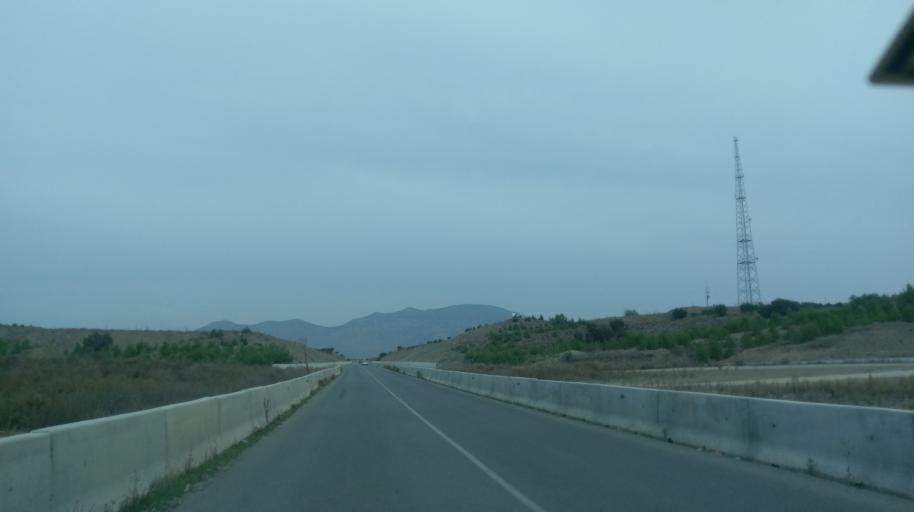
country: CY
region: Lefkosia
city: Nicosia
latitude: 35.2374
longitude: 33.3258
